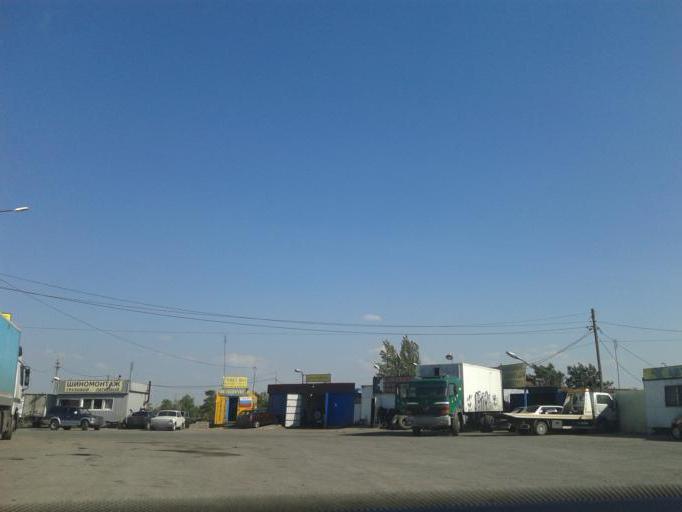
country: RU
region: Volgograd
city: Ilovlya
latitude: 49.3263
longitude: 44.0189
